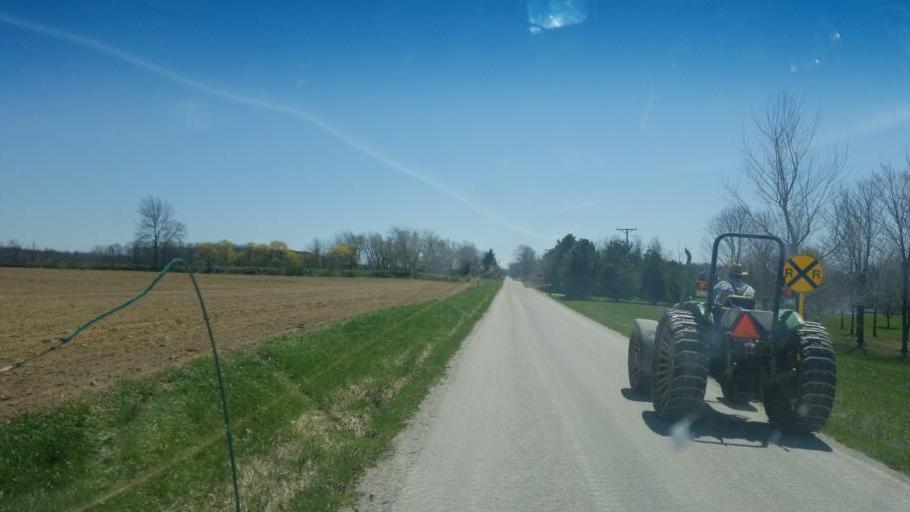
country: US
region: Ohio
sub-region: Huron County
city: Greenwich
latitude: 41.0465
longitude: -82.4598
